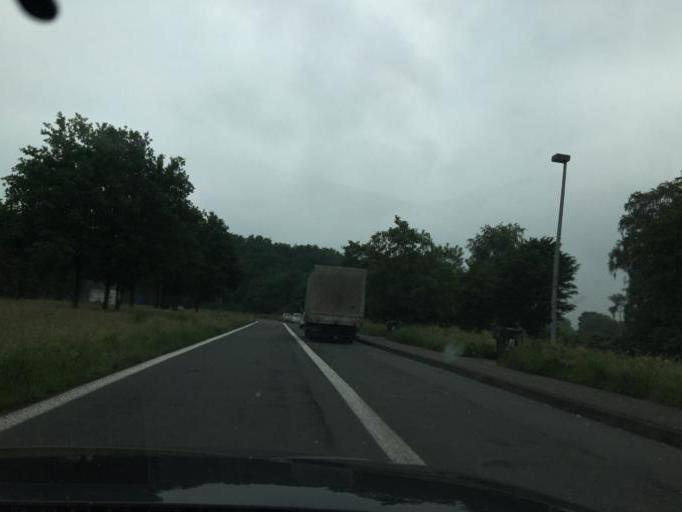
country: DE
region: North Rhine-Westphalia
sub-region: Regierungsbezirk Munster
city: Recklinghausen
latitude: 51.6384
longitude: 7.1711
